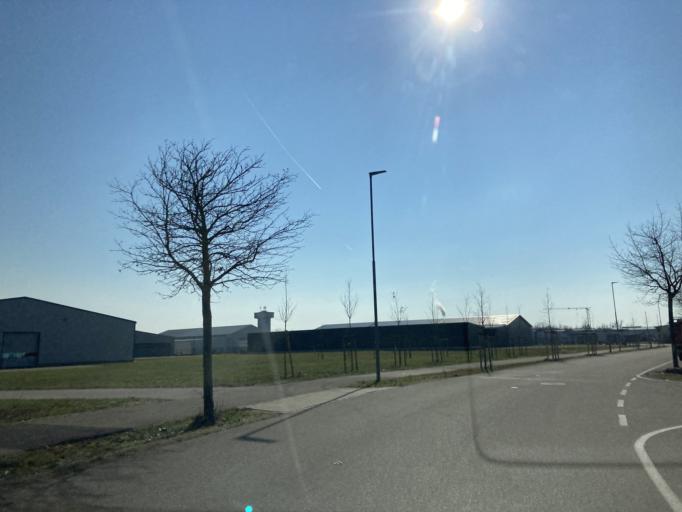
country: DE
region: Baden-Wuerttemberg
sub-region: Freiburg Region
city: Eschbach
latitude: 47.8995
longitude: 7.6242
